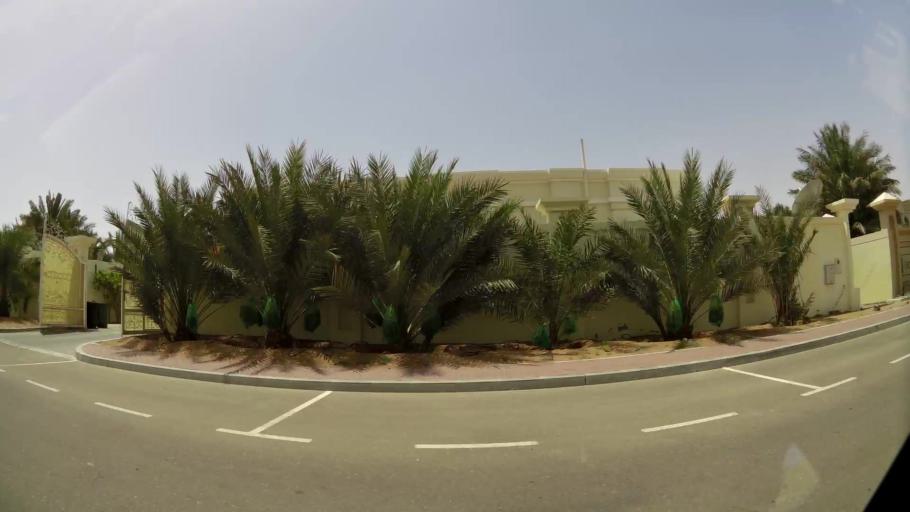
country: AE
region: Abu Dhabi
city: Al Ain
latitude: 24.1835
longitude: 55.7185
